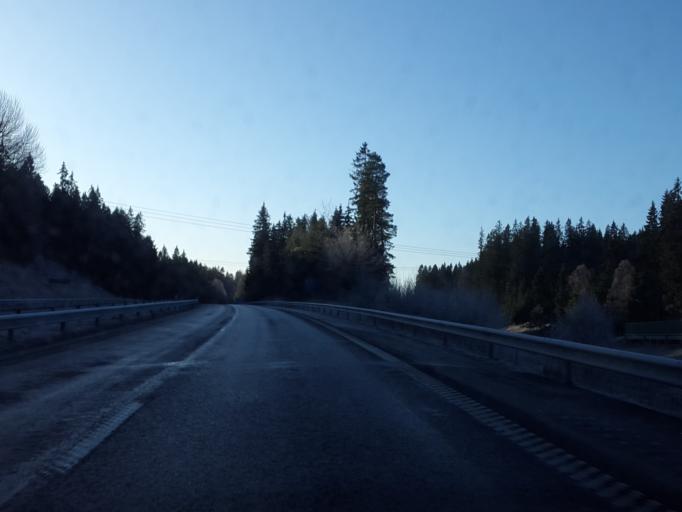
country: SE
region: Vaestra Goetaland
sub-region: Alingsas Kommun
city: Ingared
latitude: 57.8842
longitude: 12.4899
